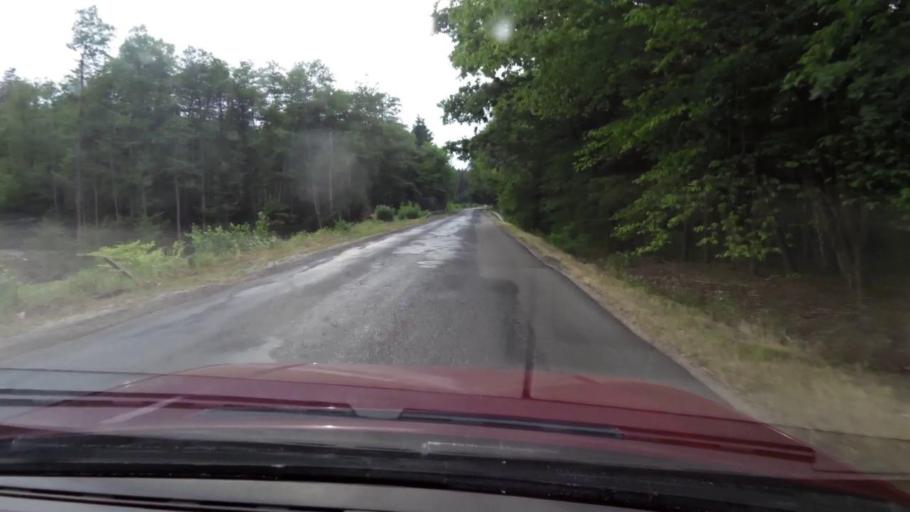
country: PL
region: Pomeranian Voivodeship
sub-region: Powiat slupski
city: Kepice
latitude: 54.2687
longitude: 16.9981
